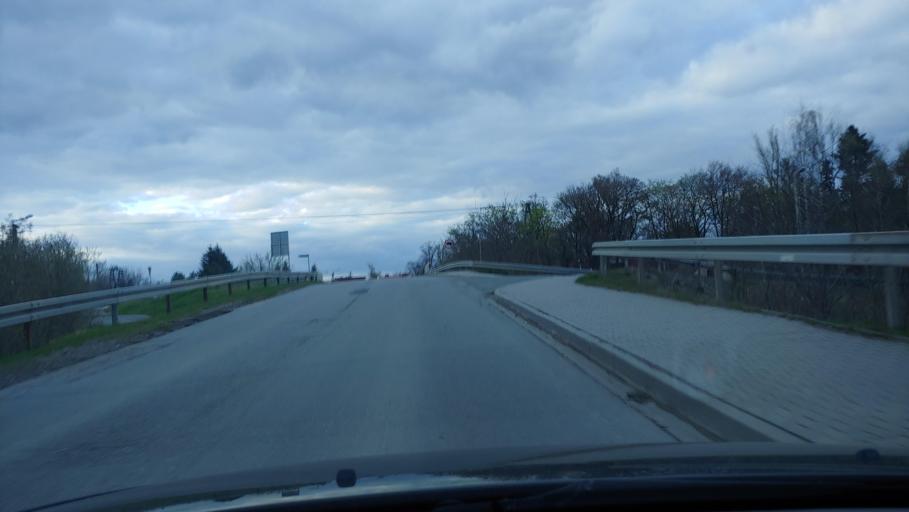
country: PL
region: Lesser Poland Voivodeship
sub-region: Powiat krakowski
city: Rudawa
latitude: 50.1181
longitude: 19.7132
